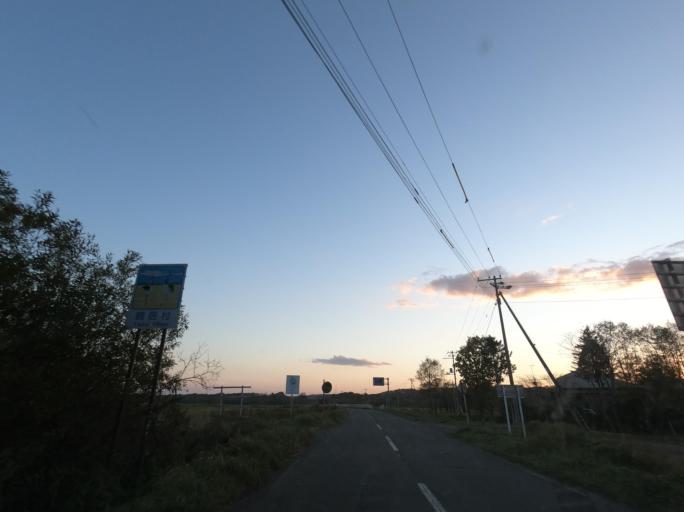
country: JP
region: Hokkaido
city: Kushiro
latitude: 43.2258
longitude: 144.4351
